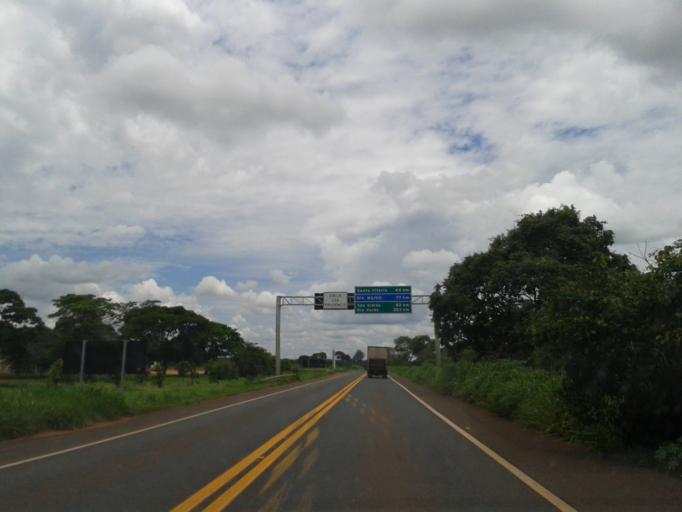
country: BR
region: Minas Gerais
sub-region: Santa Vitoria
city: Santa Vitoria
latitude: -18.9302
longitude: -49.8411
